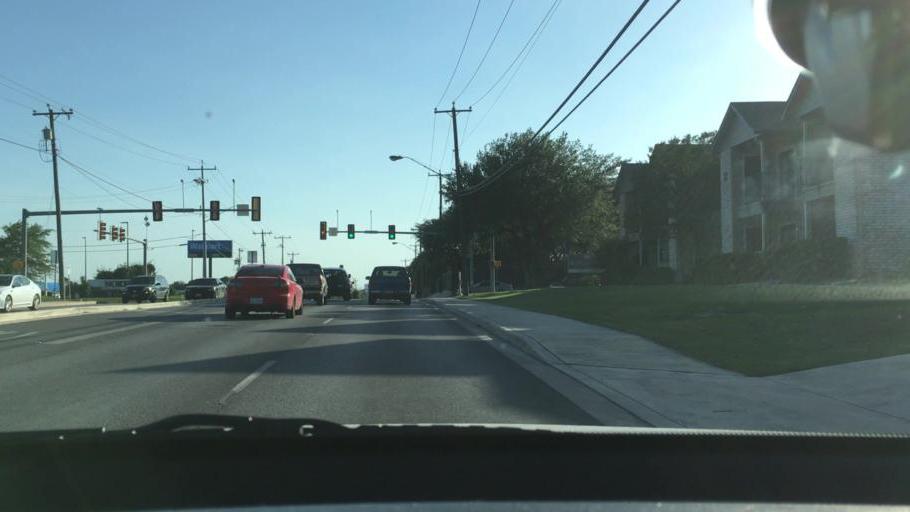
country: US
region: Texas
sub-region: Bexar County
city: Universal City
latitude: 29.5506
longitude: -98.3078
